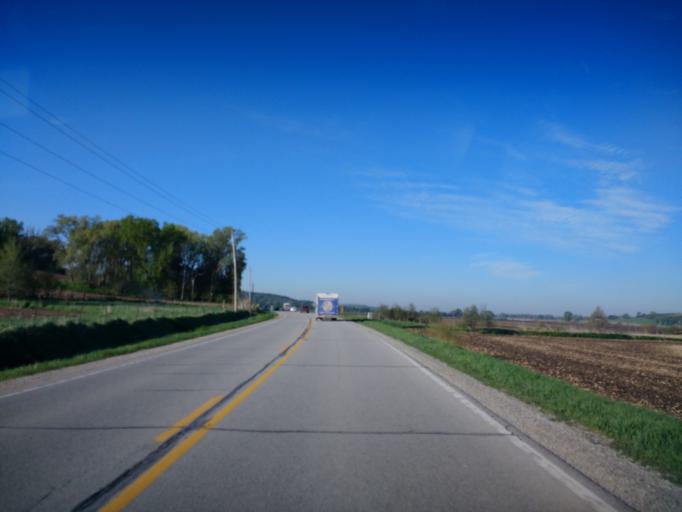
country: US
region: Iowa
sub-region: Pottawattamie County
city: Carter Lake
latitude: 41.3983
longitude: -95.8394
